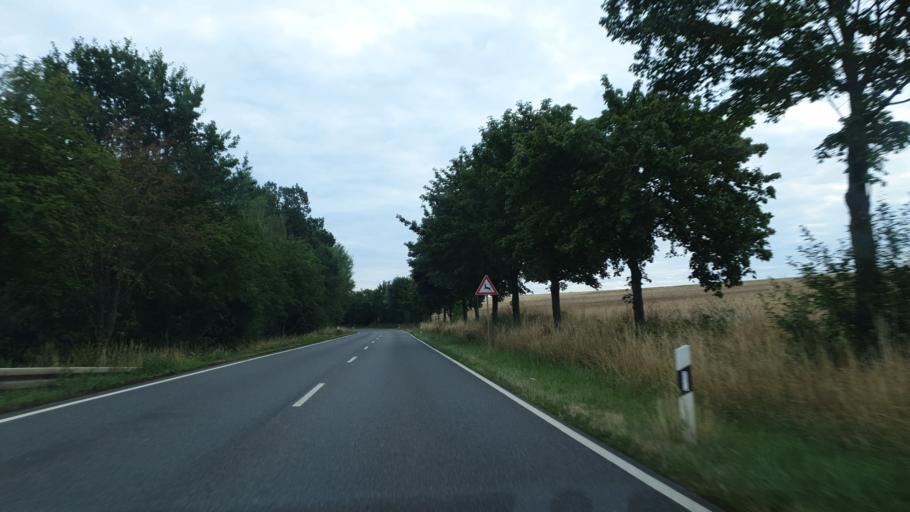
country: DE
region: Saxony
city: Sankt Egidien
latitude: 50.8013
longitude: 12.6202
